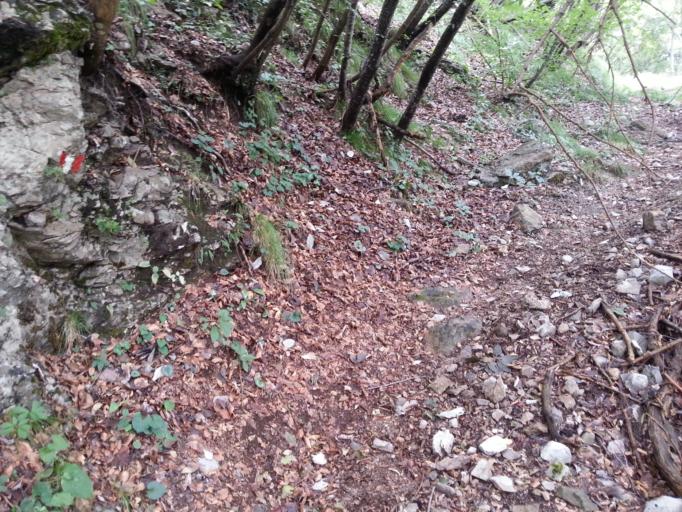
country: IT
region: Lombardy
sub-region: Provincia di Lecco
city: Cortenova
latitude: 45.9918
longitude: 9.3791
